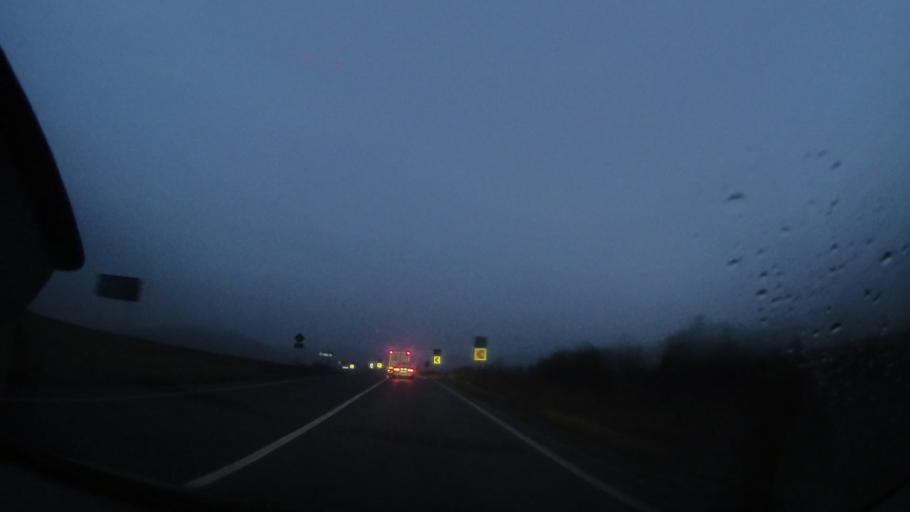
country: RO
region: Harghita
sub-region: Comuna Ditrau
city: Ditrau
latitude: 46.8313
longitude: 25.4924
